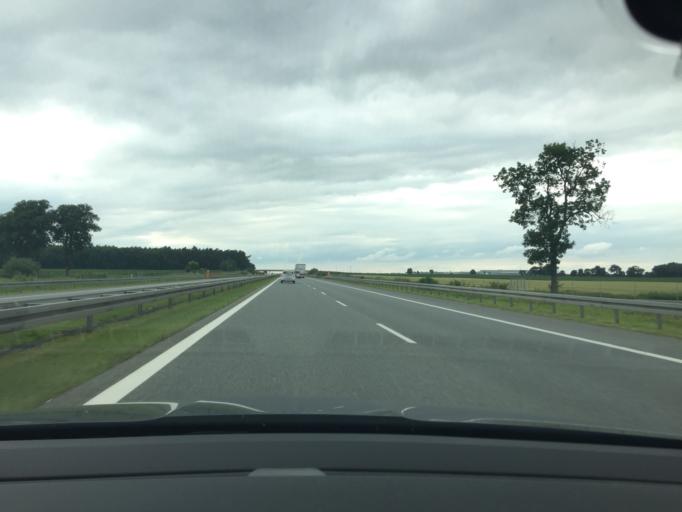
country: PL
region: Greater Poland Voivodeship
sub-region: Powiat poznanski
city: Dopiewo
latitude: 52.3613
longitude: 16.6083
